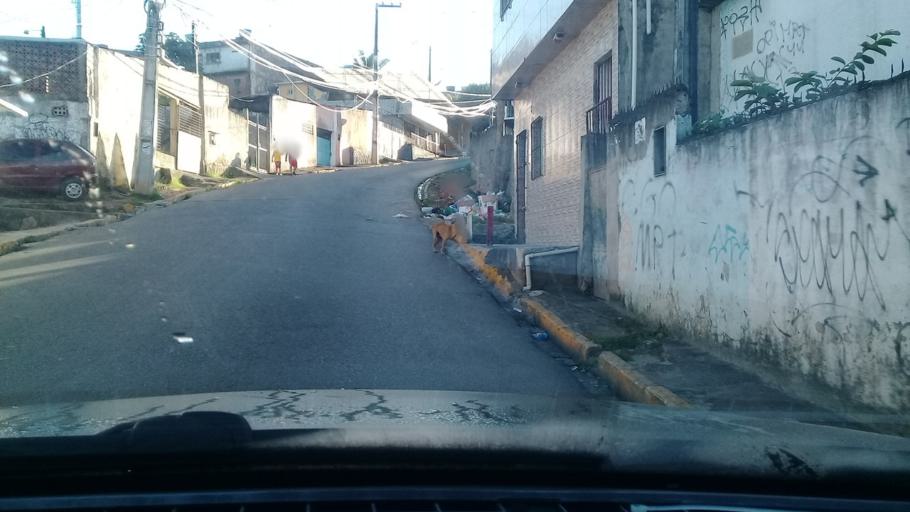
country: BR
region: Pernambuco
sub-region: Jaboatao Dos Guararapes
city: Jaboatao dos Guararapes
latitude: -8.1231
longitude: -34.9560
